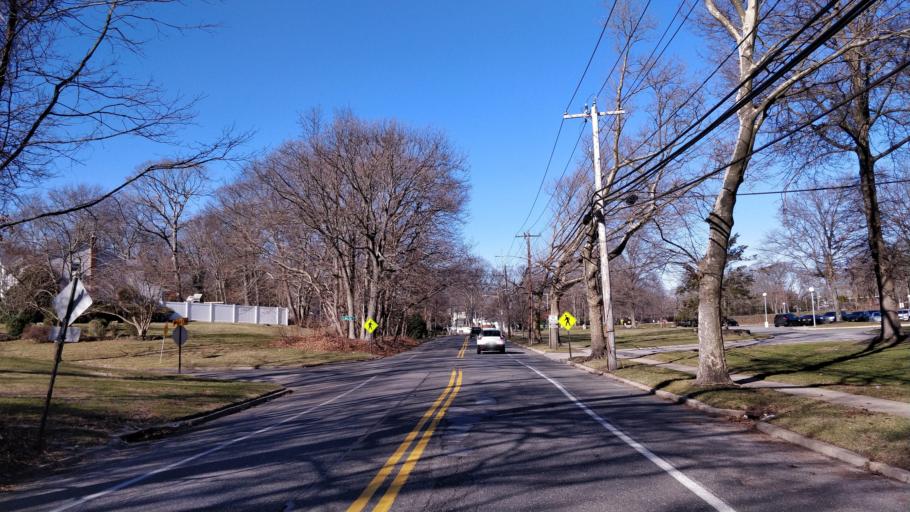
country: US
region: New York
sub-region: Suffolk County
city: Saint James
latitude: 40.8788
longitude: -73.1415
